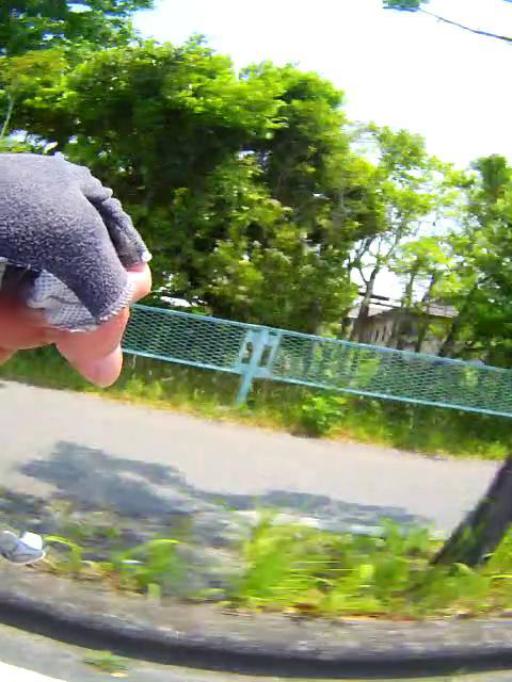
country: JP
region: Osaka
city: Mino
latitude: 34.8149
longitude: 135.4932
